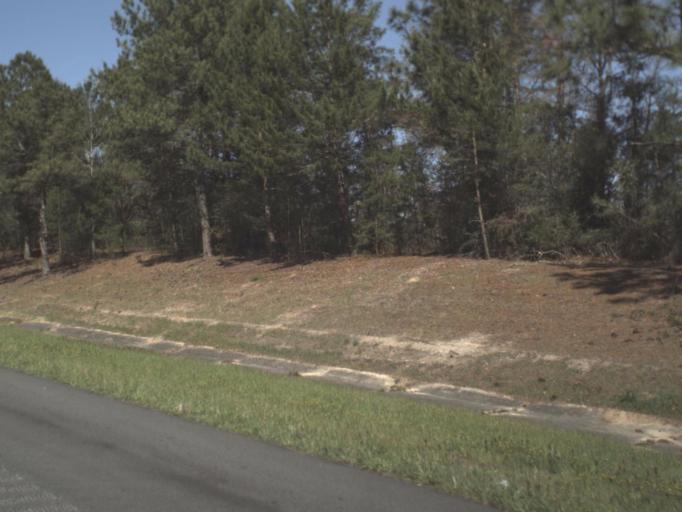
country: US
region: Florida
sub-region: Walton County
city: DeFuniak Springs
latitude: 30.6959
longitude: -85.9969
